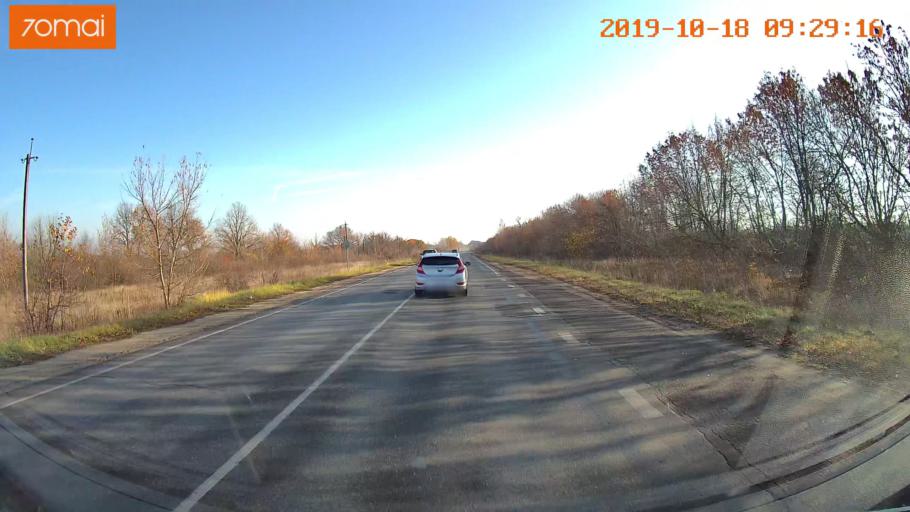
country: RU
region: Tula
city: Yefremov
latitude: 53.1368
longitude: 38.1519
